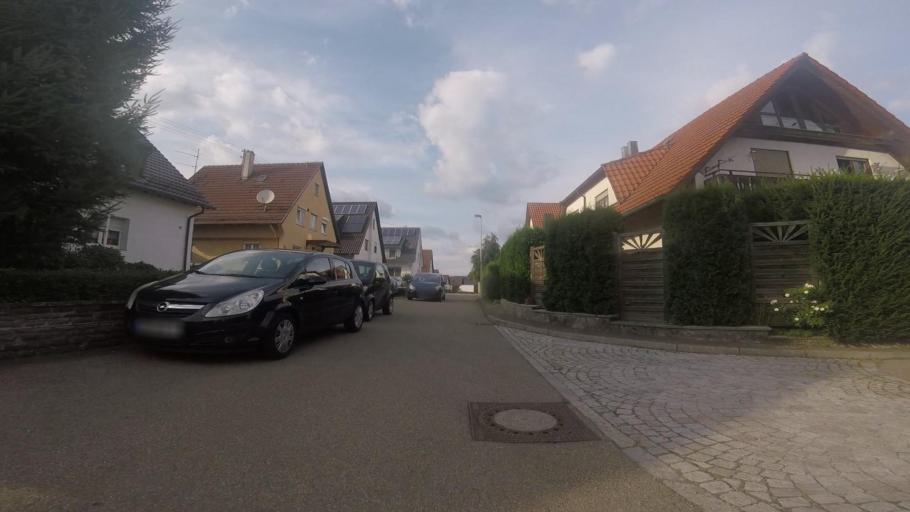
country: DE
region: Baden-Wuerttemberg
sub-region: Regierungsbezirk Stuttgart
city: Aspach
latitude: 48.9677
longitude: 9.3890
